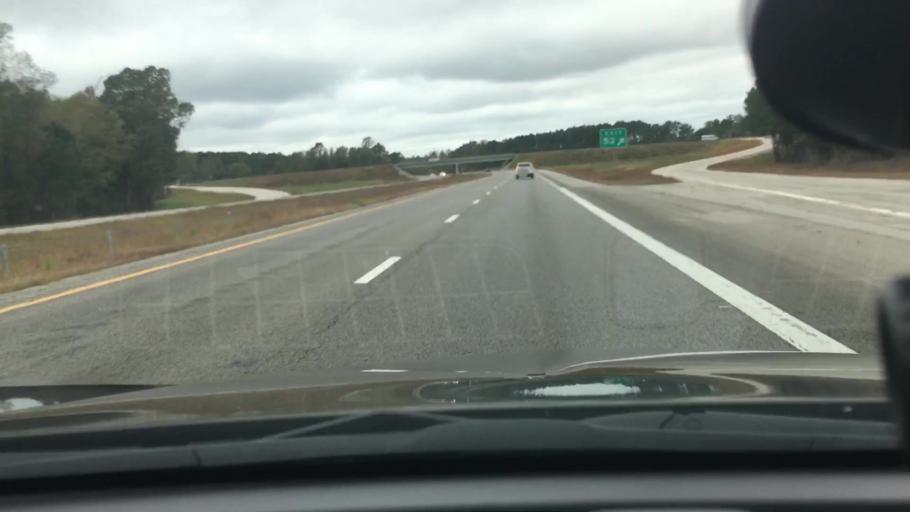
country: US
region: North Carolina
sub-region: Wilson County
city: Wilson
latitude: 35.6657
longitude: -77.7605
